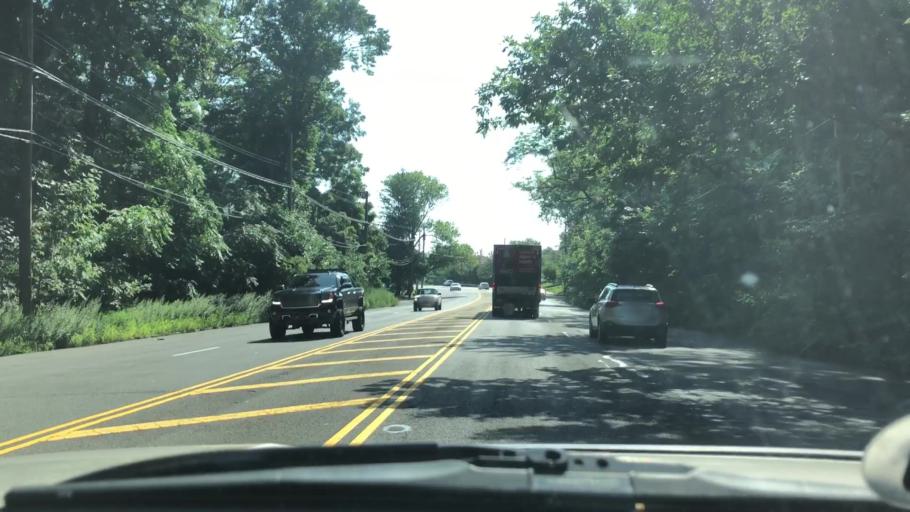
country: US
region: New York
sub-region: Richmond County
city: Staten Island
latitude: 40.5266
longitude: -74.1706
